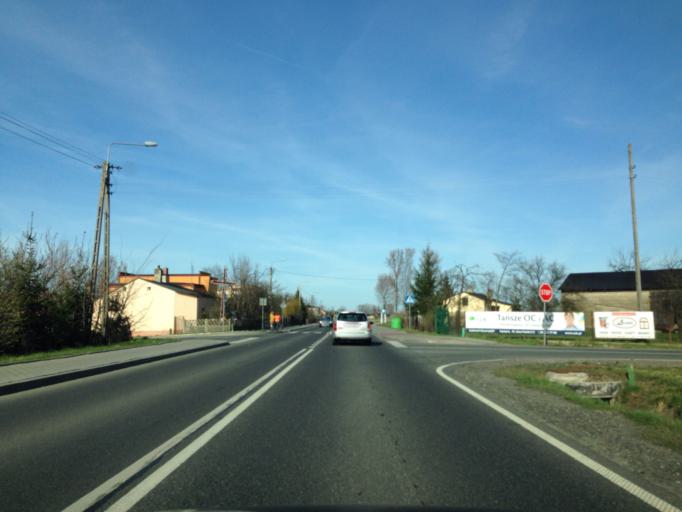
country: PL
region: Lodz Voivodeship
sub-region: Powiat leczycki
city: Leczyca
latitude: 52.0362
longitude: 19.1295
